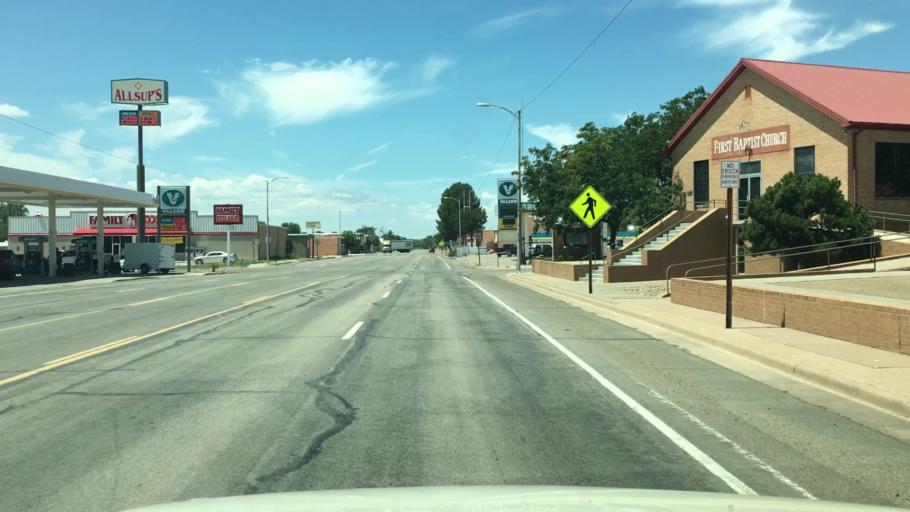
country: US
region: New Mexico
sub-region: De Baca County
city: Fort Sumner
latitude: 34.4708
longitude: -104.2423
